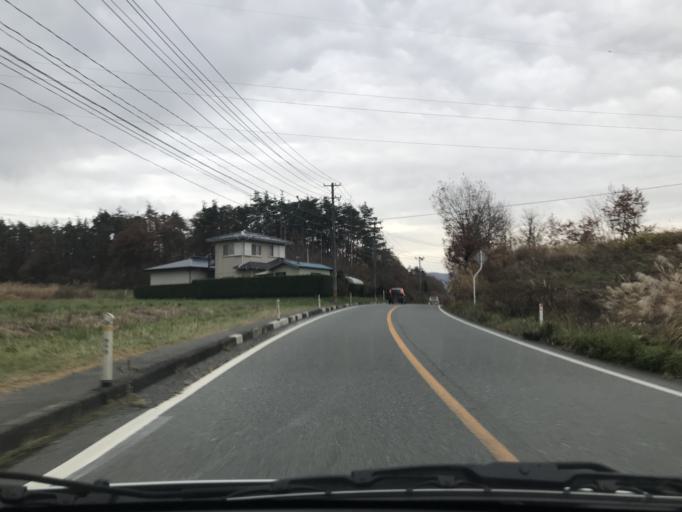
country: JP
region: Iwate
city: Ichinoseki
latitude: 39.0047
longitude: 141.3262
